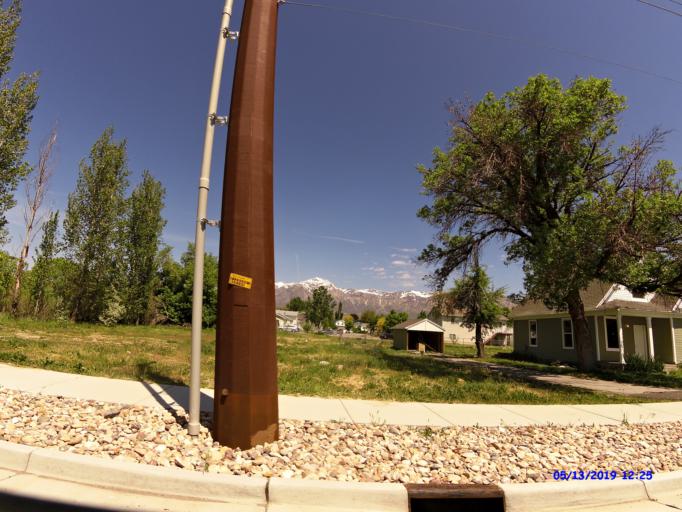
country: US
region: Utah
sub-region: Weber County
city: Harrisville
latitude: 41.2666
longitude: -111.9661
